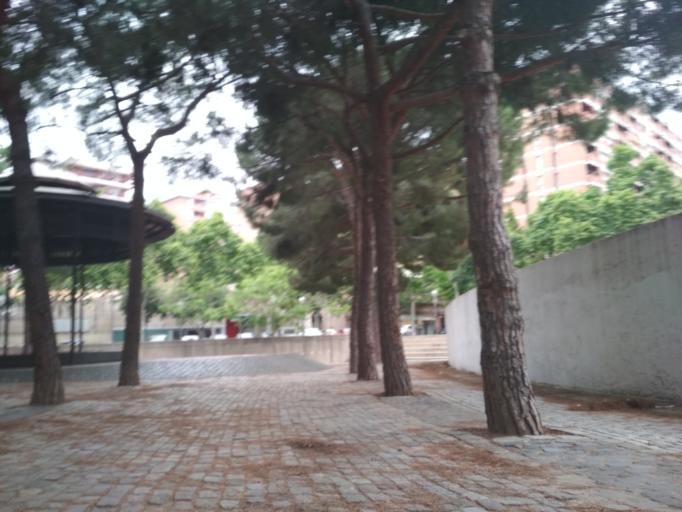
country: ES
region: Catalonia
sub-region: Provincia de Barcelona
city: Sant Marti
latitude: 41.4197
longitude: 2.2047
